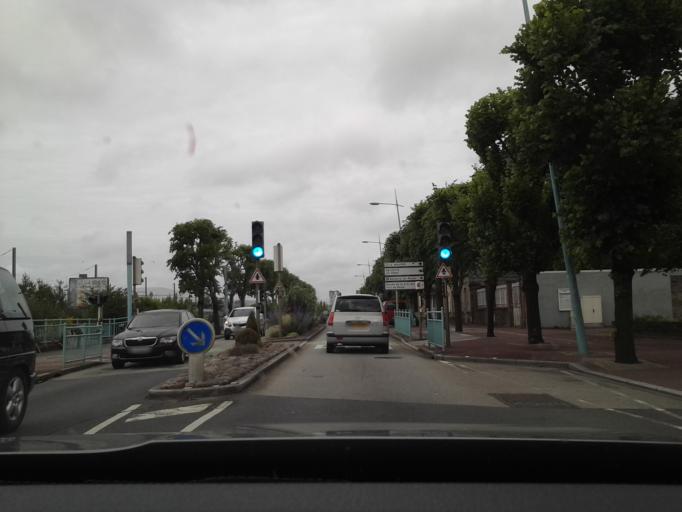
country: FR
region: Lower Normandy
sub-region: Departement de la Manche
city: Cherbourg-Octeville
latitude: 49.6308
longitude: -1.6178
